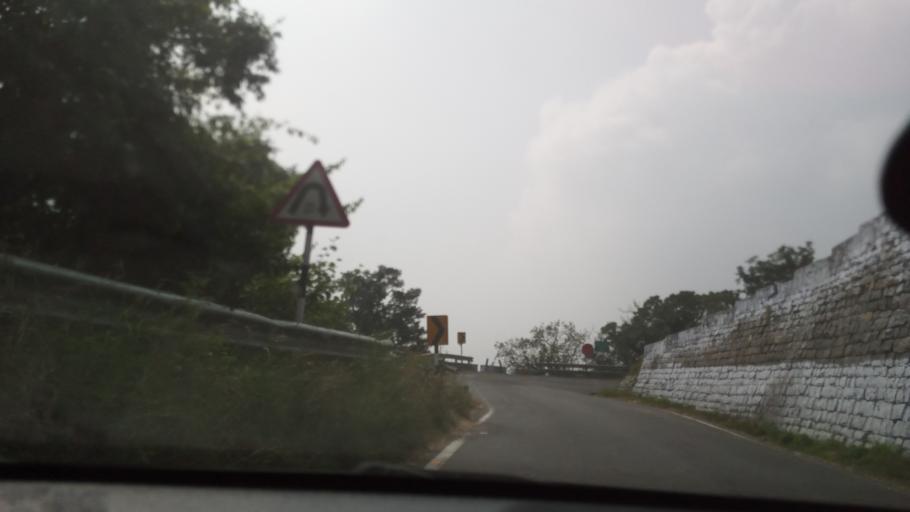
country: IN
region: Tamil Nadu
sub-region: Erode
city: Sathyamangalam
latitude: 11.5948
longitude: 77.1258
